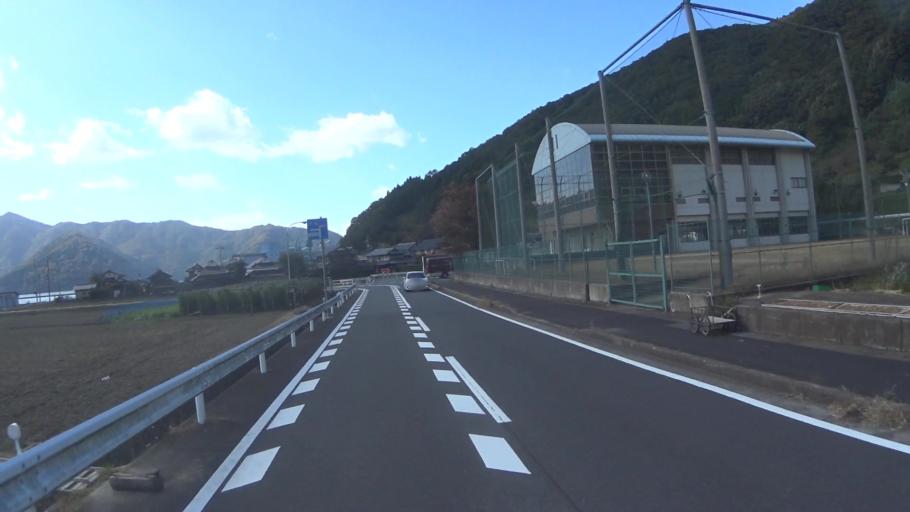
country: JP
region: Kyoto
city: Maizuru
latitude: 35.5213
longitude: 135.3567
